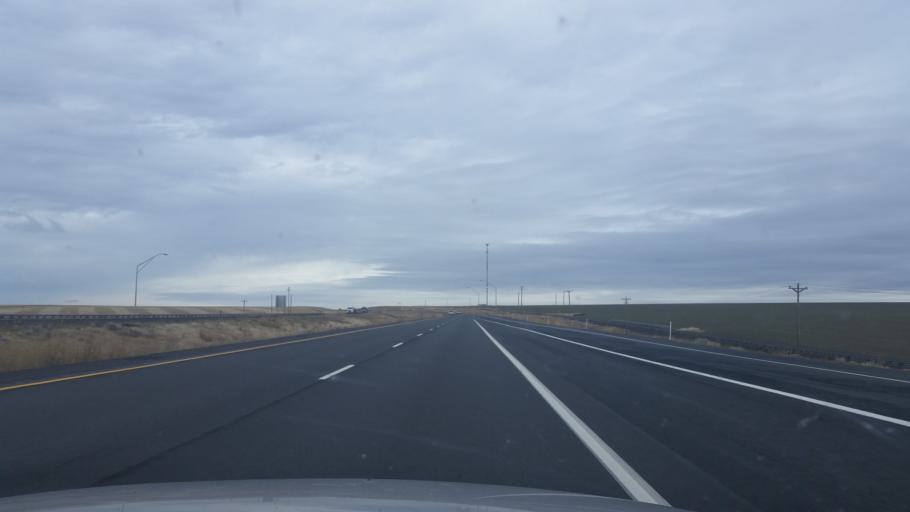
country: US
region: Washington
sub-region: Adams County
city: Ritzville
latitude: 47.0974
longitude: -118.6725
